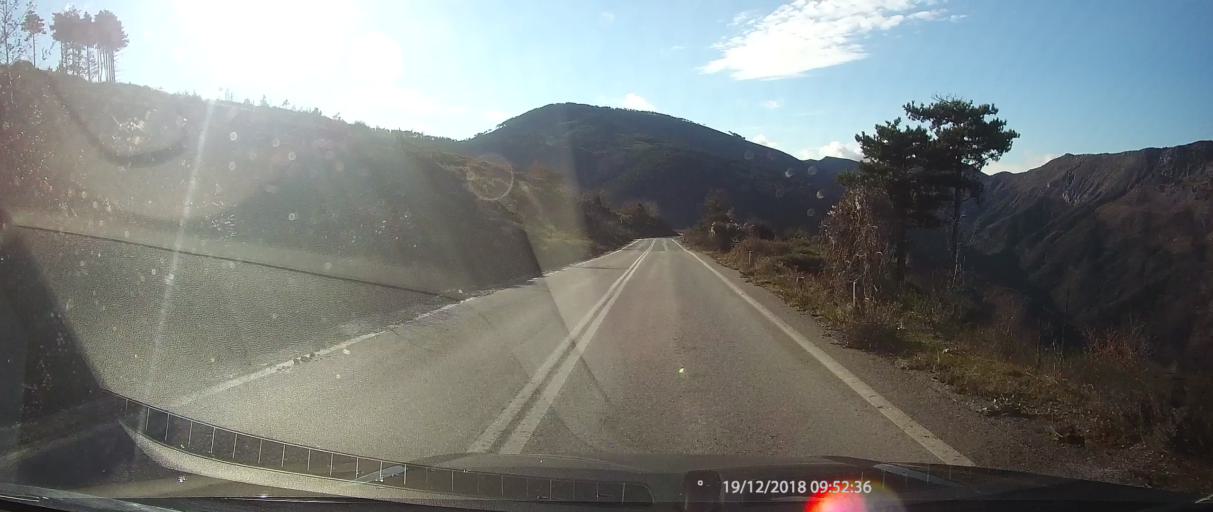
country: GR
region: Peloponnese
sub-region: Nomos Messinias
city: Paralia Vergas
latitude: 37.0729
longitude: 22.2547
